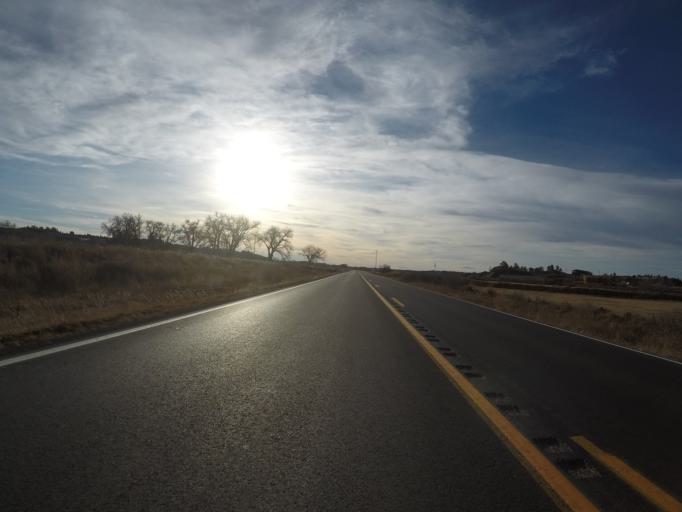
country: US
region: Montana
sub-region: Musselshell County
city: Roundup
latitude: 46.3673
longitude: -108.6504
